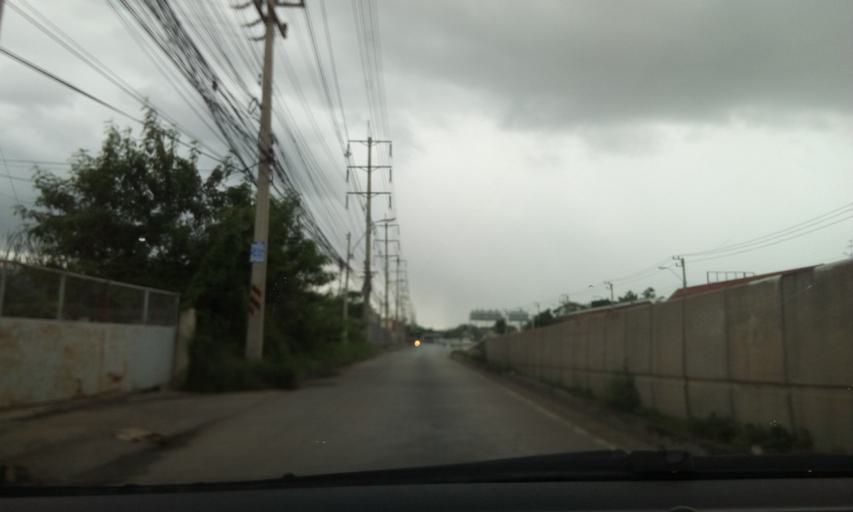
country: TH
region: Phra Nakhon Si Ayutthaya
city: Ban Bang Kadi Pathum Thani
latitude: 13.9644
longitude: 100.5508
